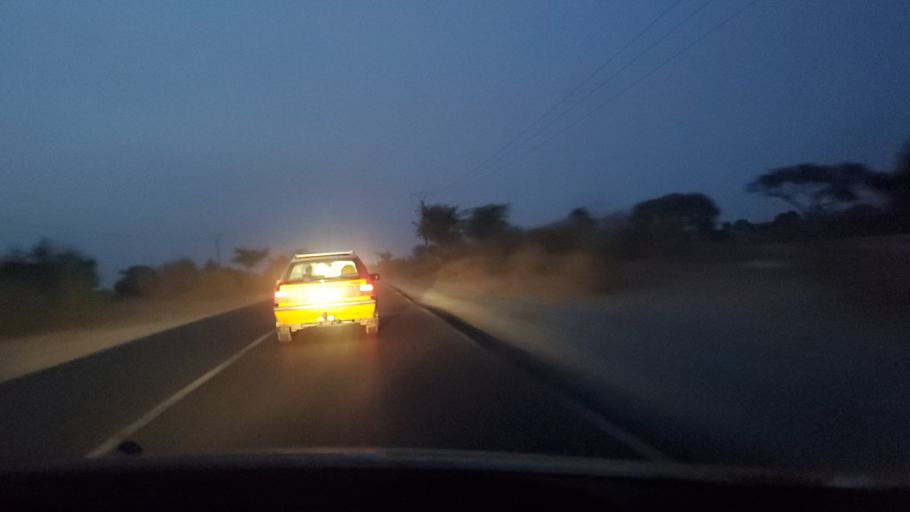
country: SN
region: Louga
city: Louga
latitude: 15.7196
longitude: -16.2720
